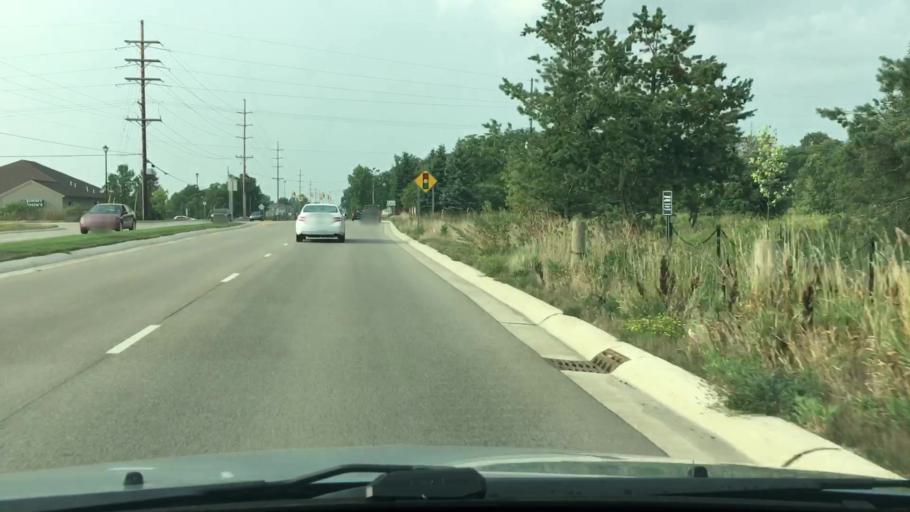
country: US
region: Michigan
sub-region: Ottawa County
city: Allendale
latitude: 42.9704
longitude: -85.9042
